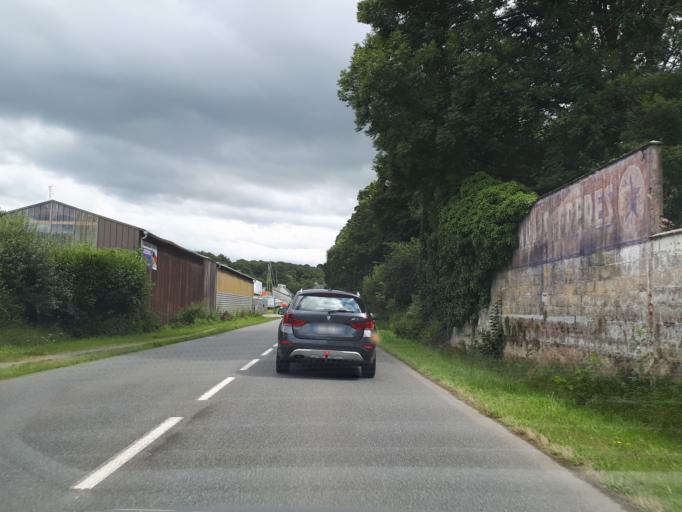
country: FR
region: Brittany
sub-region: Departement du Finistere
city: Morlaix
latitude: 48.5993
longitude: -3.8441
